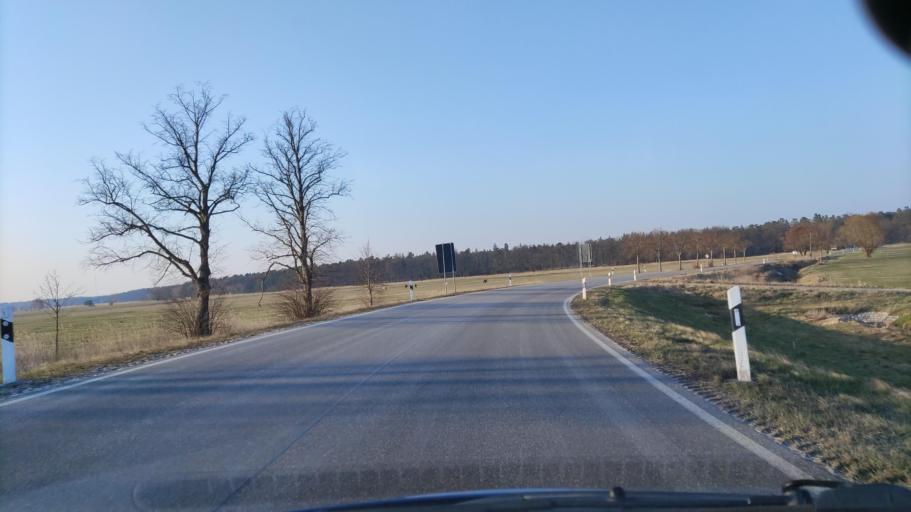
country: DE
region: Brandenburg
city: Lanz
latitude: 52.9941
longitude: 11.5487
